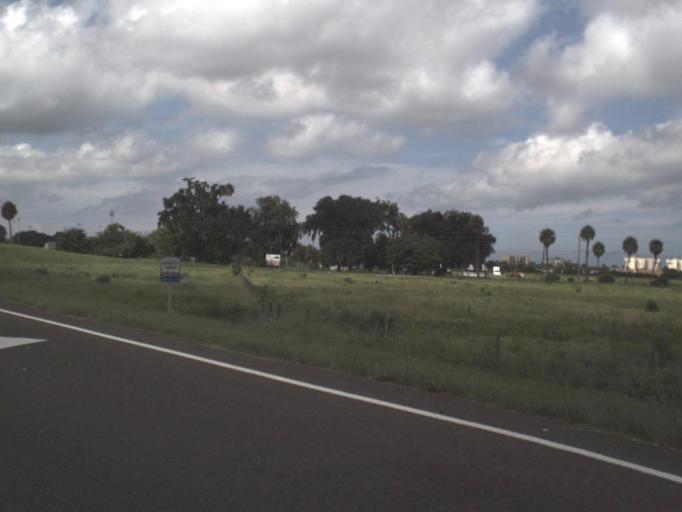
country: US
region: Florida
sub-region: Manatee County
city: Memphis
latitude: 27.5345
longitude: -82.5708
